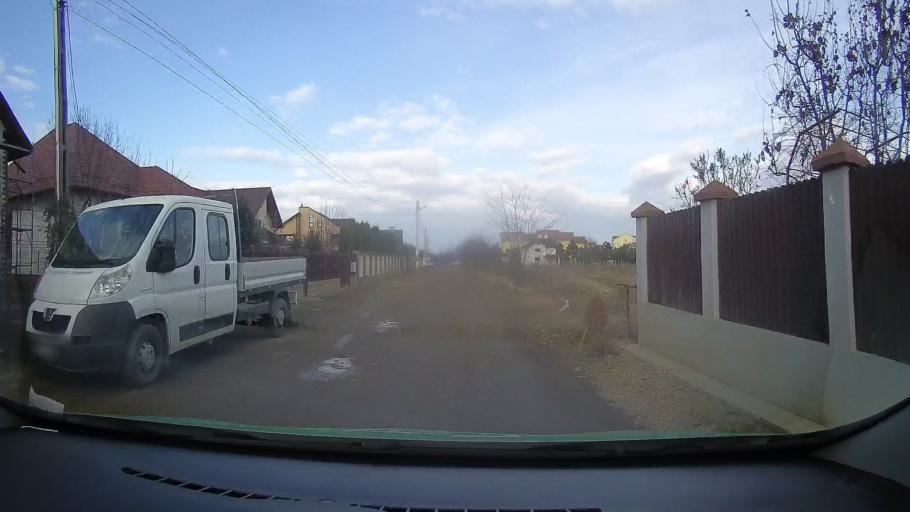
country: RO
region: Dambovita
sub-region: Comuna Ulmi
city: Ulmi
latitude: 44.8990
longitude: 25.5001
